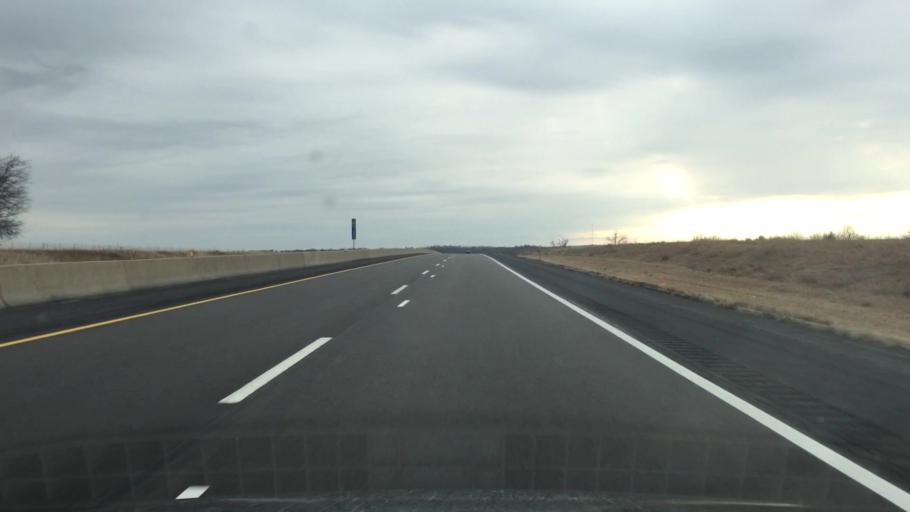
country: US
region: Kansas
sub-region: Osage County
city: Osage City
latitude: 38.6781
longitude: -96.0053
